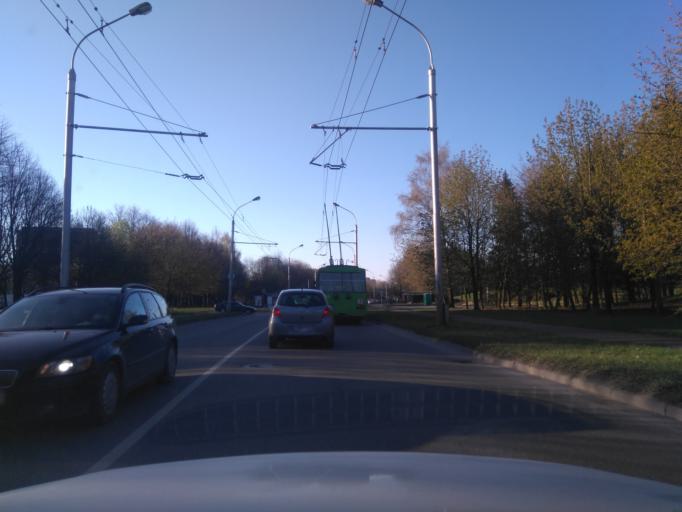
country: LT
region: Kauno apskritis
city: Dainava (Kaunas)
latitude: 54.9172
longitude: 23.9728
